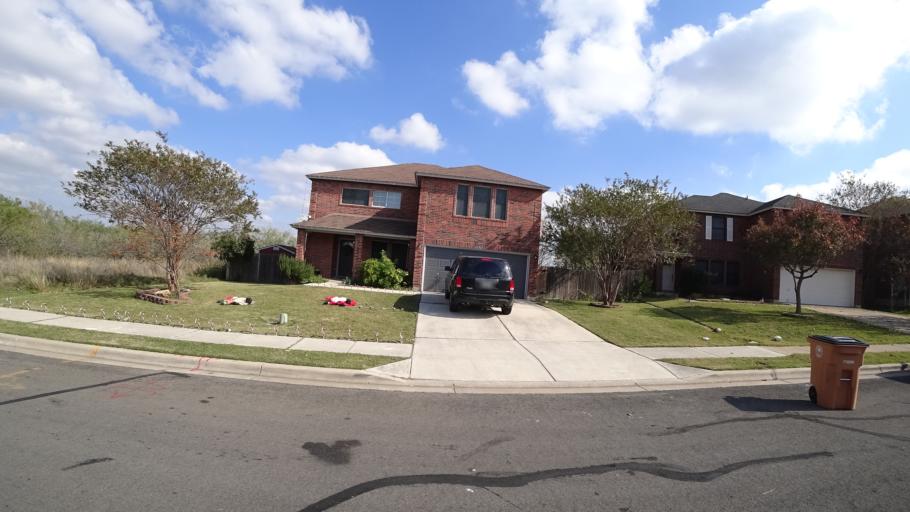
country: US
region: Texas
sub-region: Travis County
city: Shady Hollow
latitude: 30.1593
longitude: -97.8445
